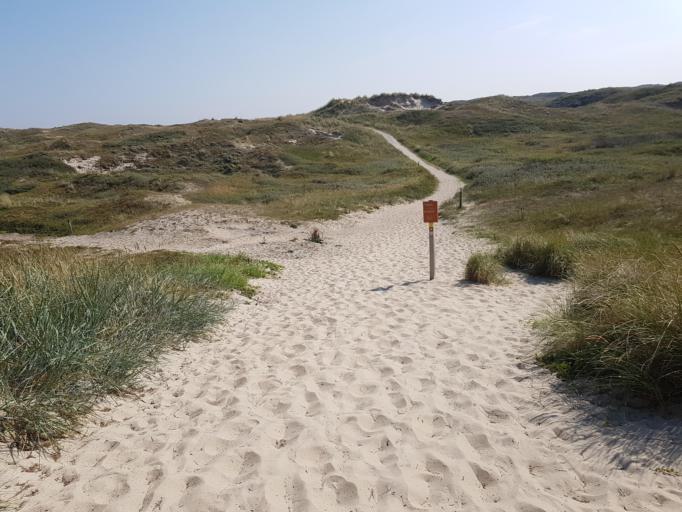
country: NL
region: North Holland
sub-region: Gemeente Texel
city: Den Burg
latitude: 53.1692
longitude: 4.8311
